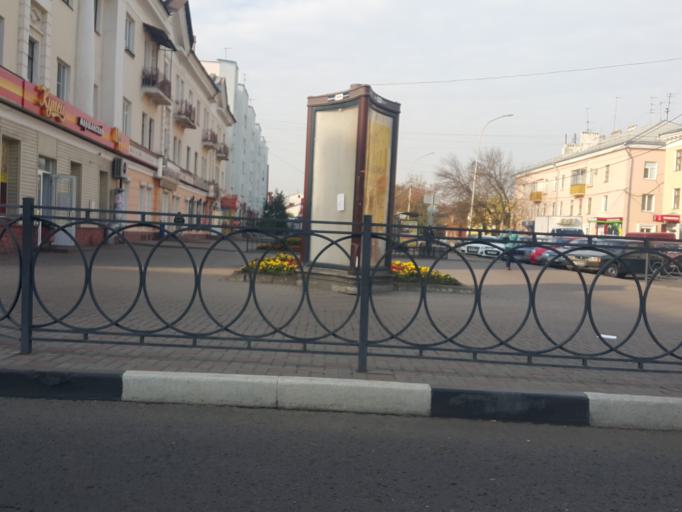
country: RU
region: Tambov
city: Tambov
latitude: 52.7256
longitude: 41.4507
